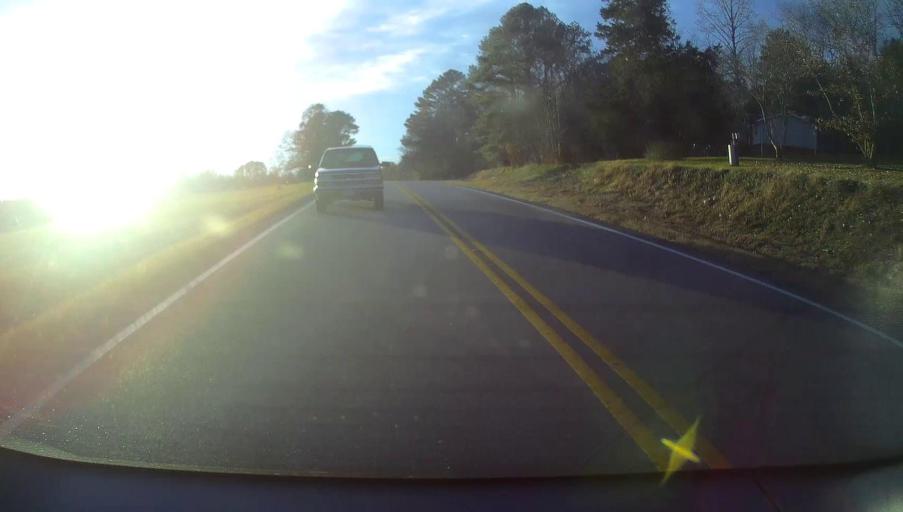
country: US
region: Alabama
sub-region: Saint Clair County
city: Steele
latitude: 34.0667
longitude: -86.2742
